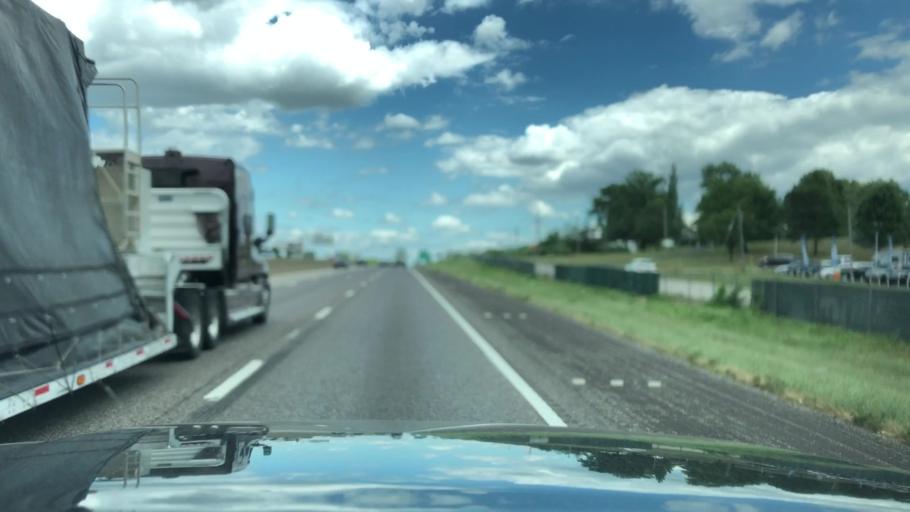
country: US
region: Missouri
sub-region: Saint Charles County
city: Lake Saint Louis
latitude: 38.8034
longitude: -90.7552
